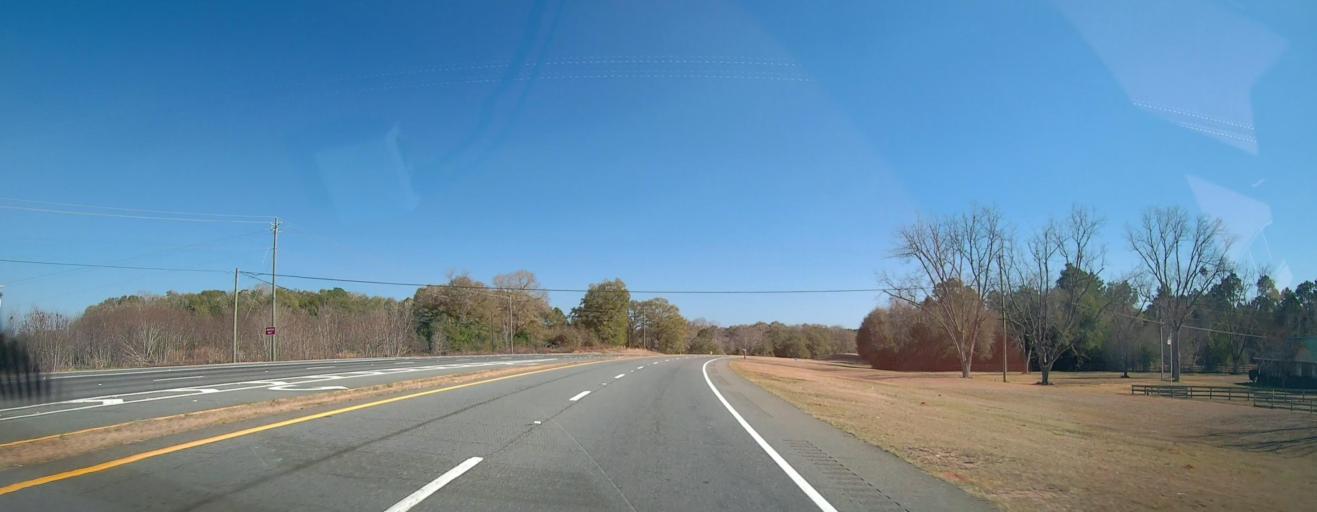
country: US
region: Georgia
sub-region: Sumter County
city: Americus
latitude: 32.1134
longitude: -84.2468
